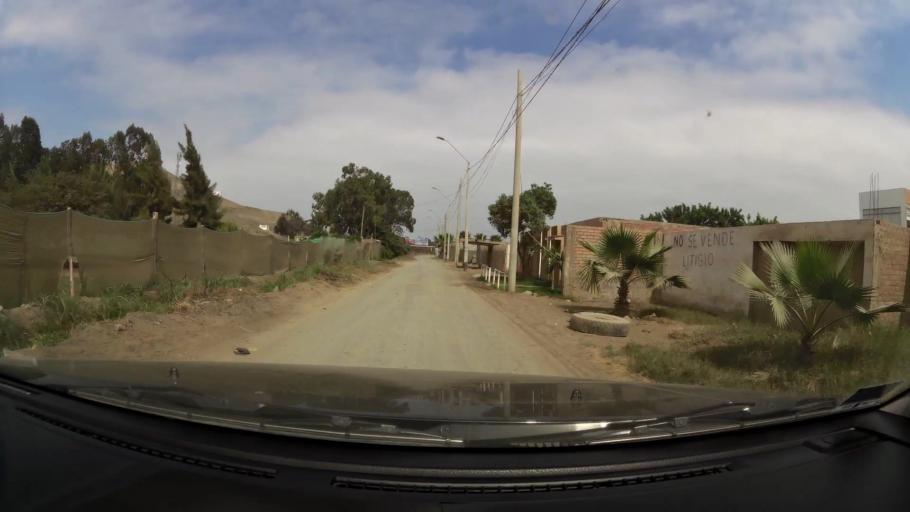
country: PE
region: Lima
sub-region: Provincia de Canete
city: Asia
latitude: -12.7342
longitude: -76.6244
